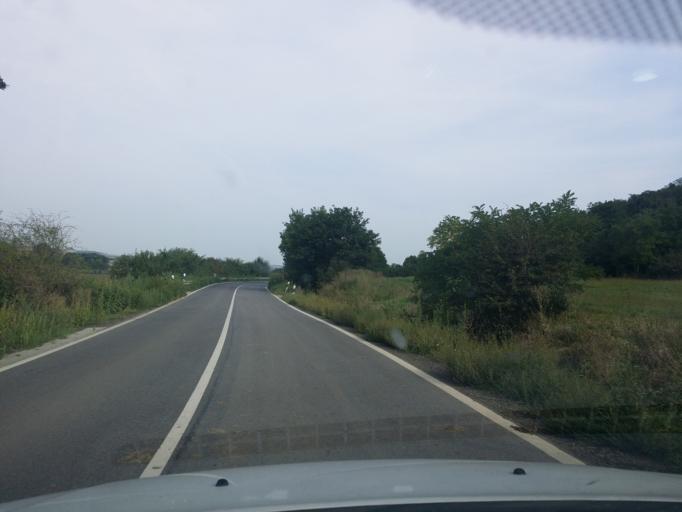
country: HU
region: Pest
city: Acsa
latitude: 47.7636
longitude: 19.3713
